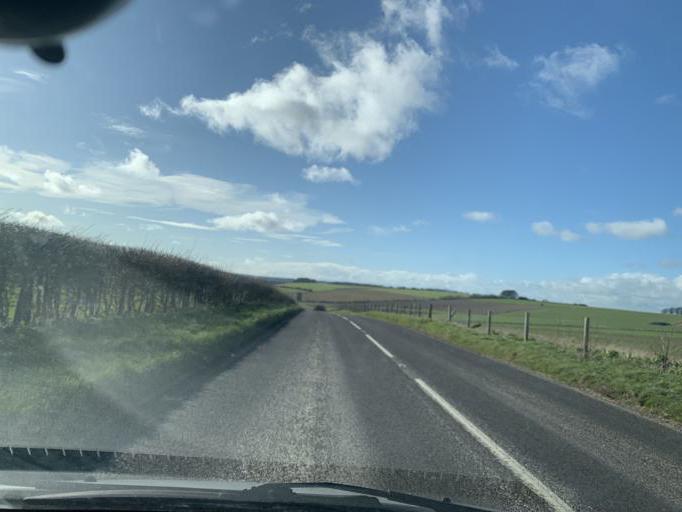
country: GB
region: England
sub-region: Wiltshire
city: Boyton
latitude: 51.1874
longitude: -2.0574
